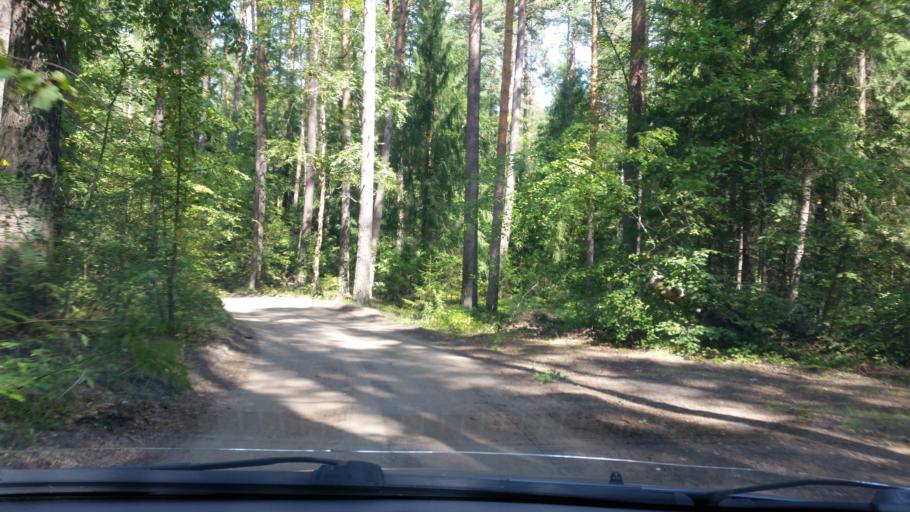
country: RU
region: Moskovskaya
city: Pushchino
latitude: 54.9068
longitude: 37.7160
